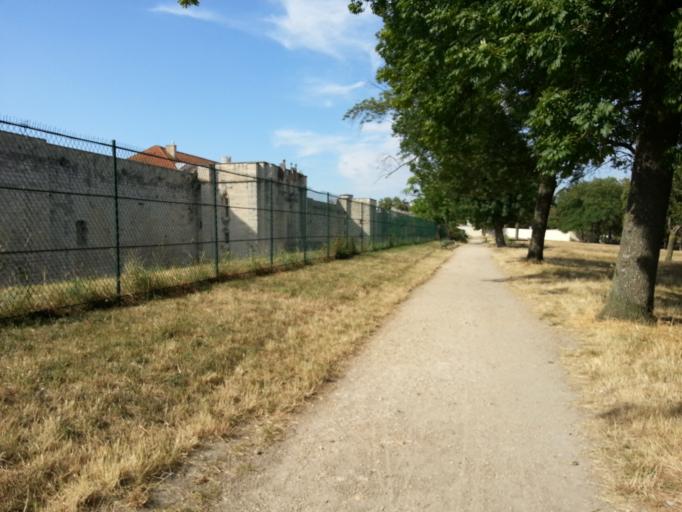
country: FR
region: Ile-de-France
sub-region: Departement du Val-de-Marne
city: Vincennes
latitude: 48.8419
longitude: 2.4376
